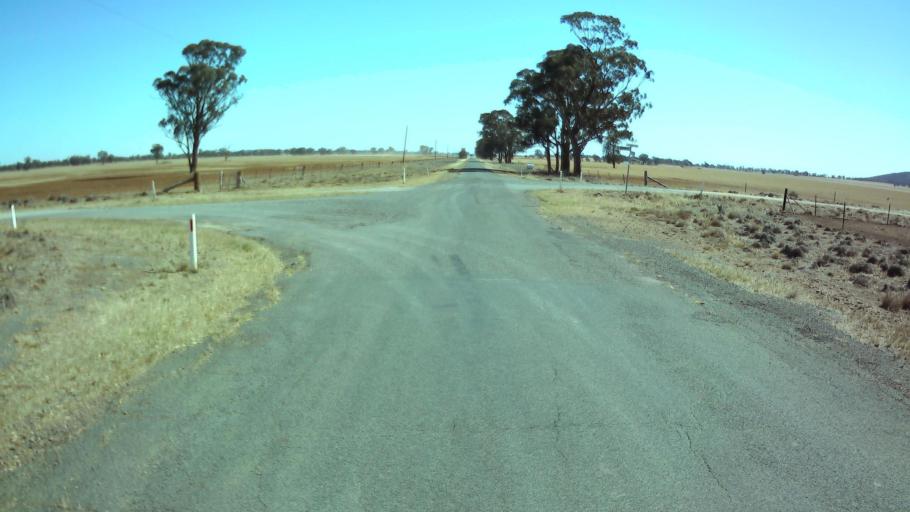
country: AU
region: New South Wales
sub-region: Weddin
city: Grenfell
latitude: -33.7040
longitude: 147.9188
